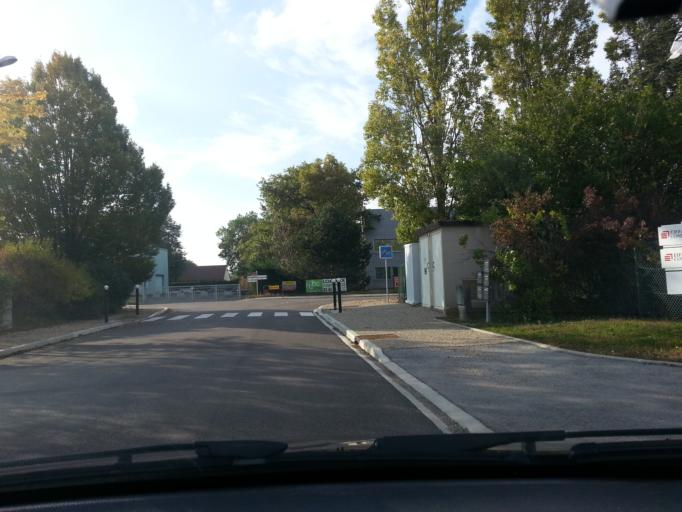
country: FR
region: Bourgogne
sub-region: Departement de Saone-et-Loire
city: Chatenoy-le-Royal
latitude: 46.7985
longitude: 4.7894
